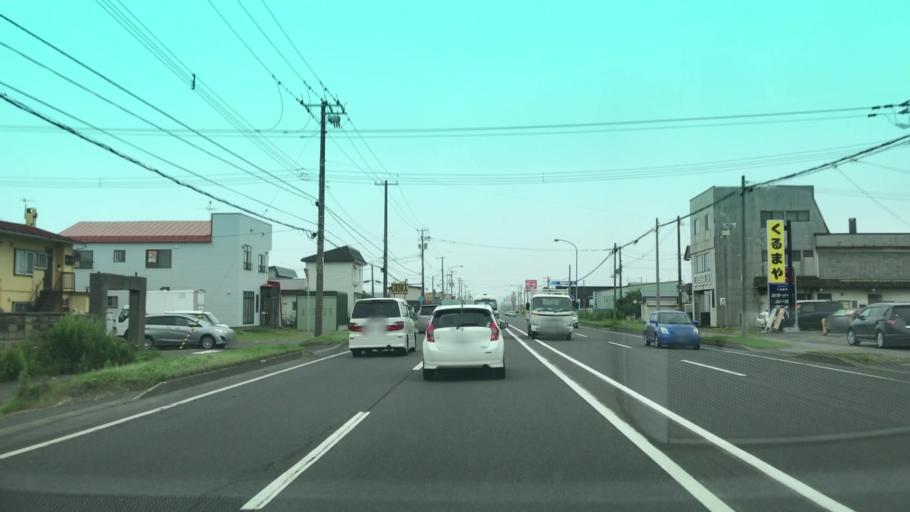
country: JP
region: Hokkaido
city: Muroran
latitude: 42.3756
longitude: 141.0684
